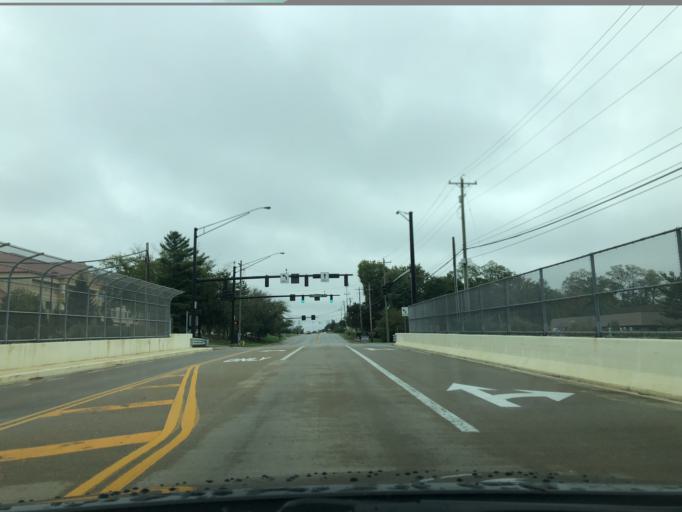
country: US
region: Ohio
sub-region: Hamilton County
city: Highpoint
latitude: 39.2833
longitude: -84.3721
